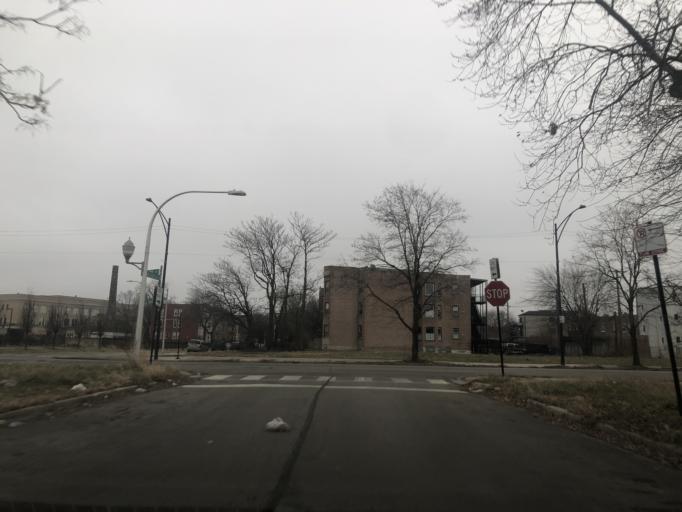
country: US
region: Illinois
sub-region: Cook County
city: Chicago
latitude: 41.7809
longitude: -87.5994
